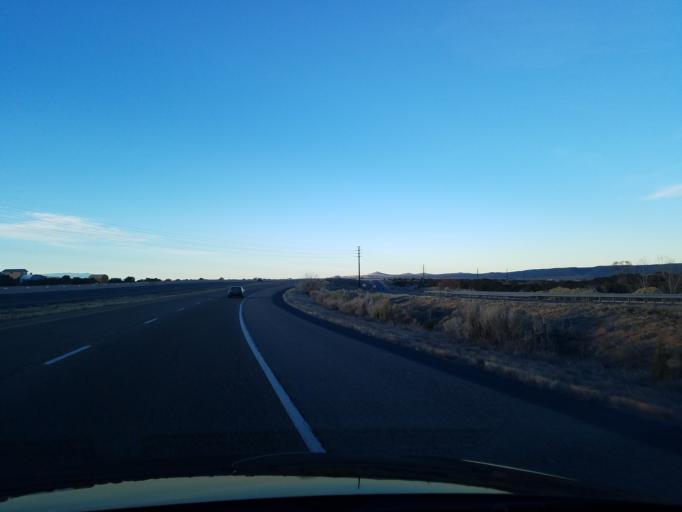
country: US
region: New Mexico
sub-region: Santa Fe County
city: Agua Fria
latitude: 35.6685
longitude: -106.0196
